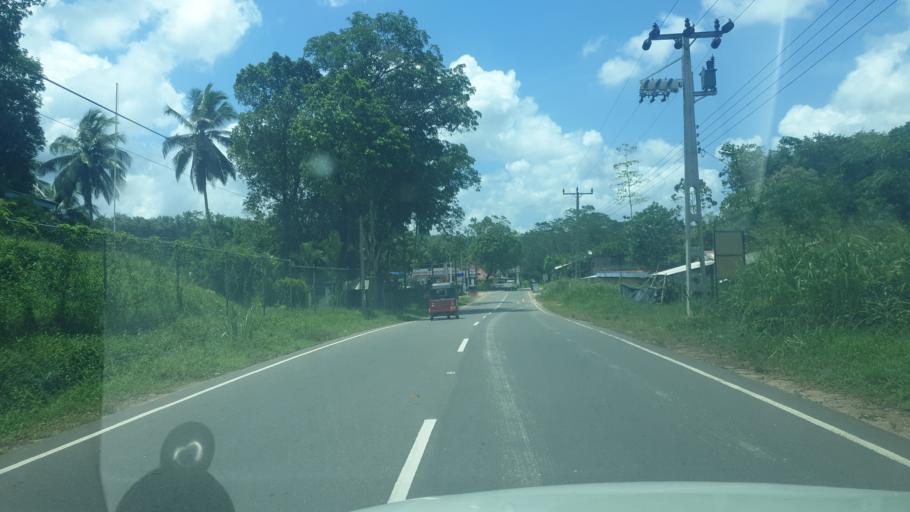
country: LK
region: Western
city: Horawala Junction
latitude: 6.5153
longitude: 80.2373
